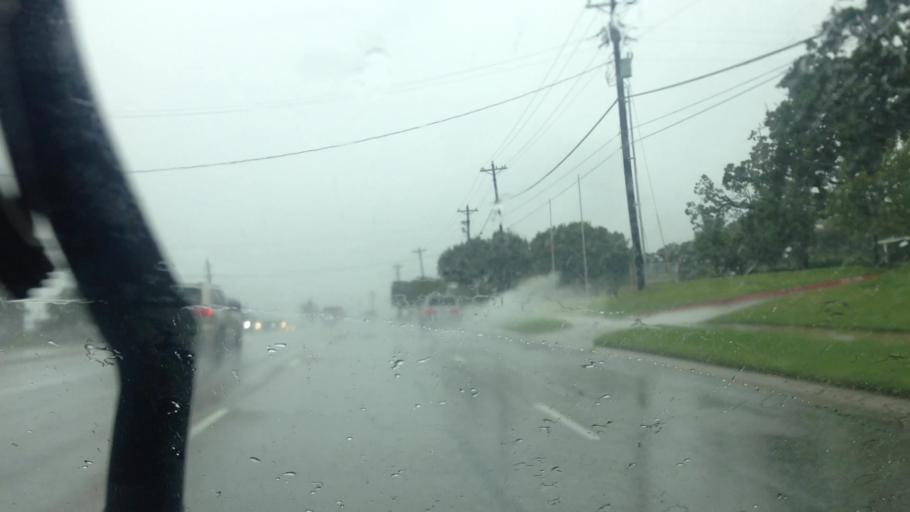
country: US
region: Texas
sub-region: Tarrant County
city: Keller
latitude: 32.9346
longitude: -97.2130
